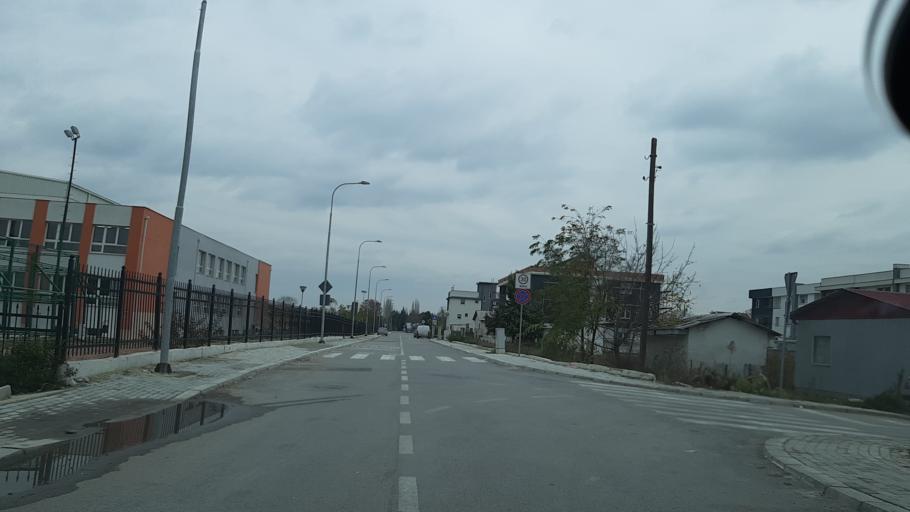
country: MK
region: Kisela Voda
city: Usje
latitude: 41.9792
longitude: 21.4702
